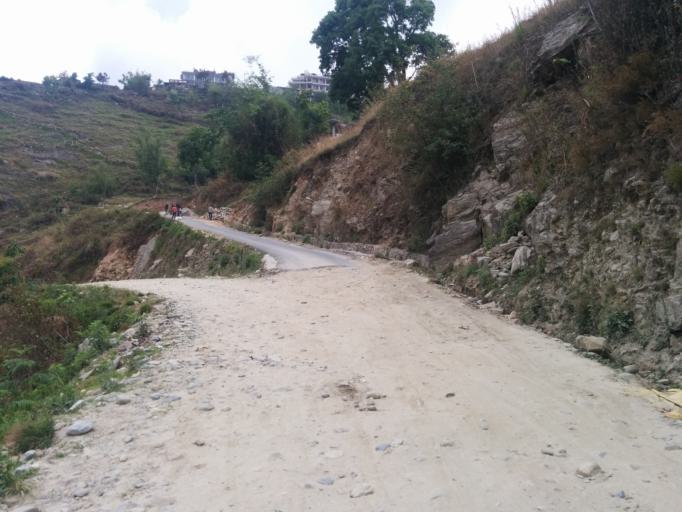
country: NP
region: Western Region
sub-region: Gandaki Zone
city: Pokhara
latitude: 28.2422
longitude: 83.9499
